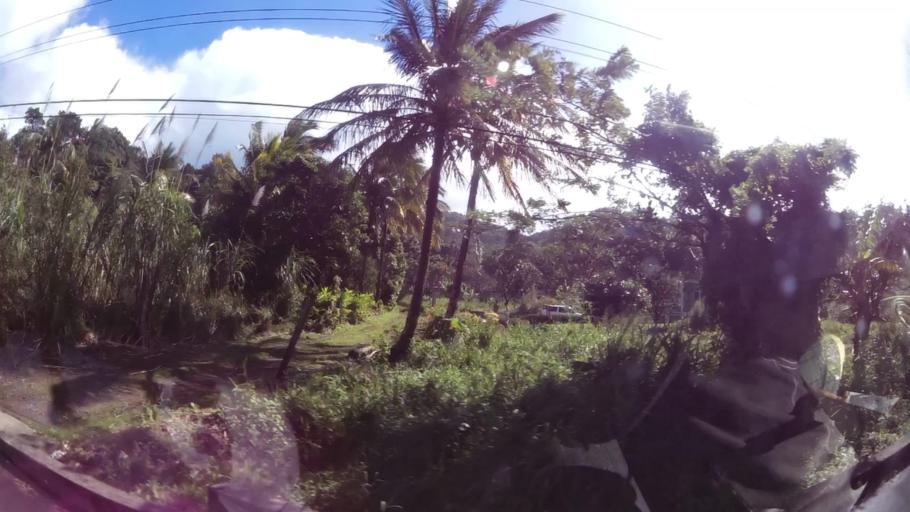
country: DM
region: Saint Paul
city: Pont Casse
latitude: 15.3655
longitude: -61.3548
